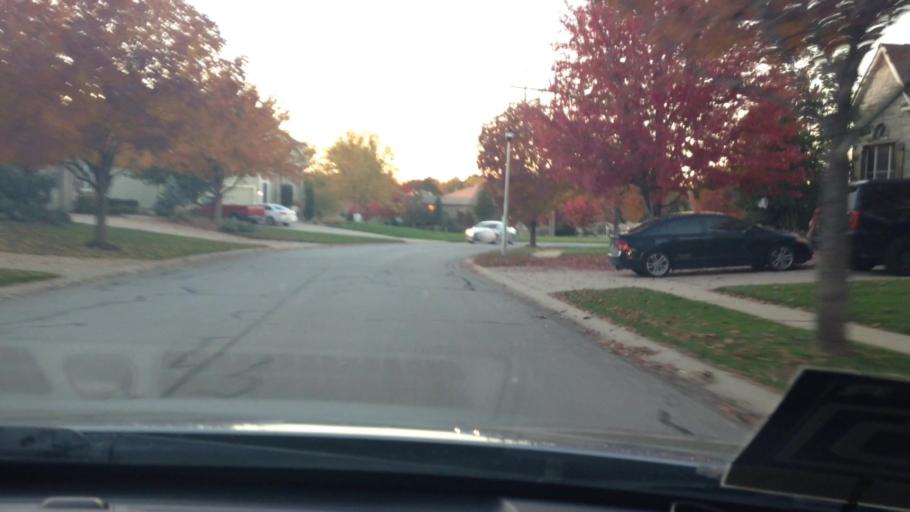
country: US
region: Kansas
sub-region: Johnson County
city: Lenexa
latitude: 38.8647
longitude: -94.7202
